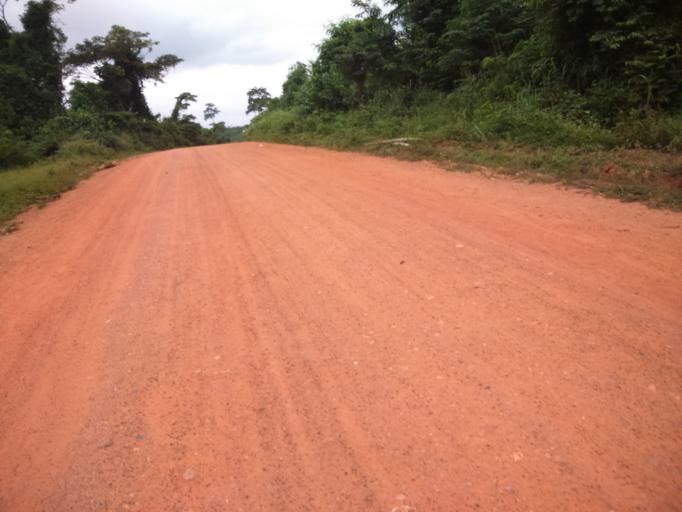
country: CI
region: Lagunes
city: Agou
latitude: 6.0823
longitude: -4.0670
